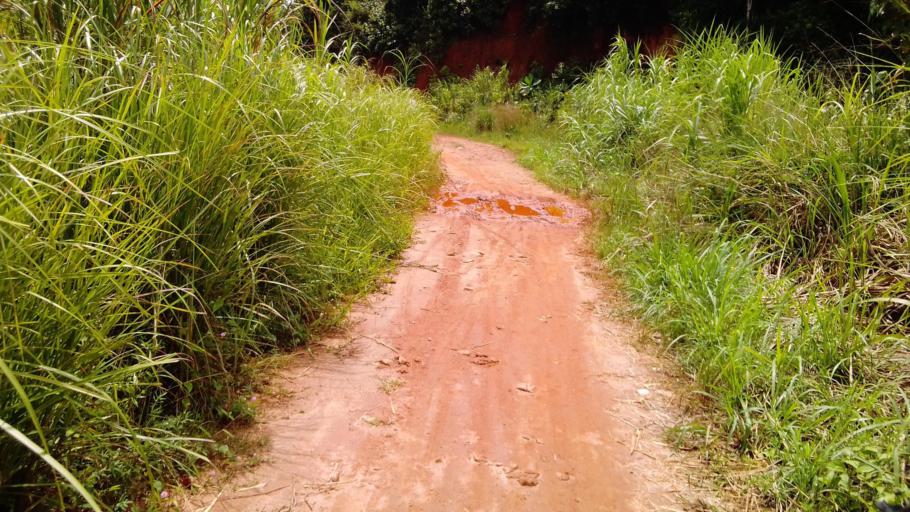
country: SL
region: Eastern Province
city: Koyima
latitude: 8.6807
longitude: -11.0048
